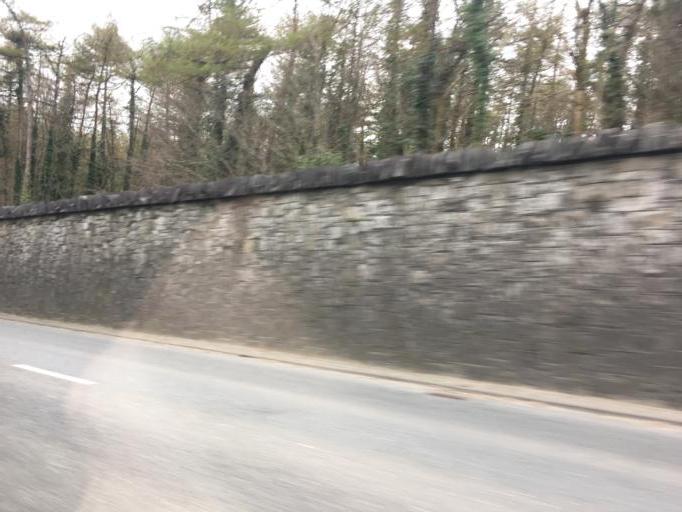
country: GB
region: Wales
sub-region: Gwynedd
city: Y Felinheli
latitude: 53.1980
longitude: -4.1821
